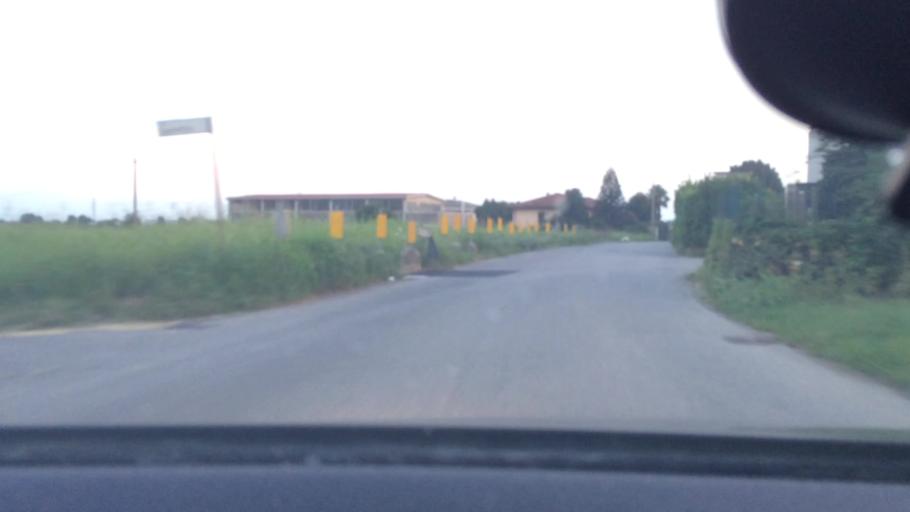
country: IT
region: Lombardy
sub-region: Provincia di Varese
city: Gerenzano
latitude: 45.6493
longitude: 8.9896
